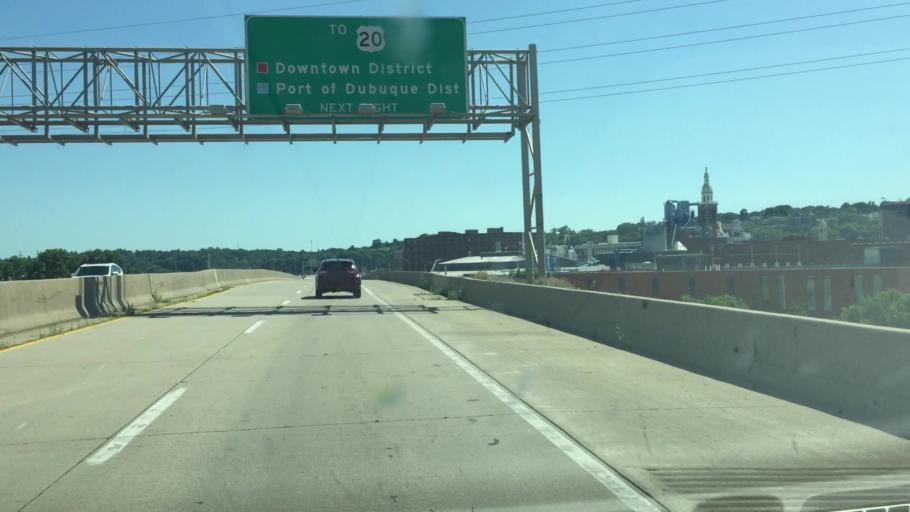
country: US
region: Iowa
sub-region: Dubuque County
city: Dubuque
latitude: 42.5051
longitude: -90.6605
